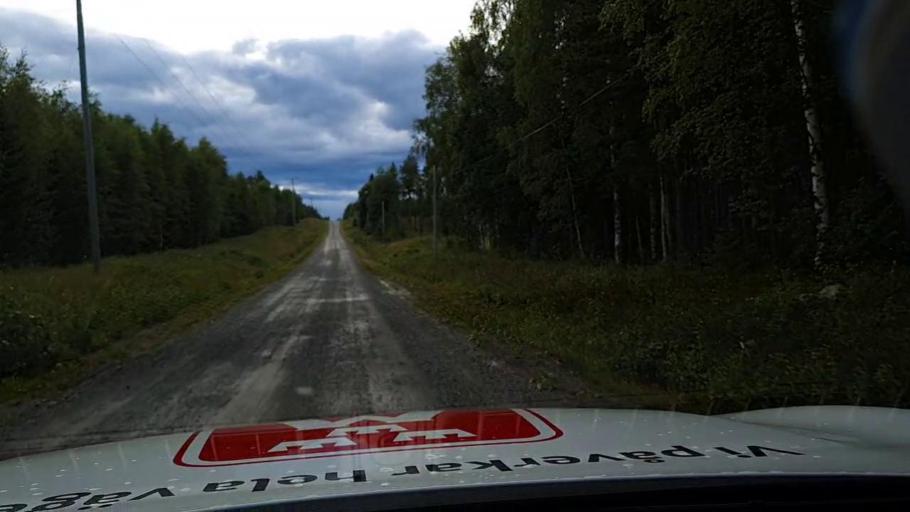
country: SE
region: Jaemtland
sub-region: Bergs Kommun
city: Hoverberg
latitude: 62.8877
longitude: 14.5748
